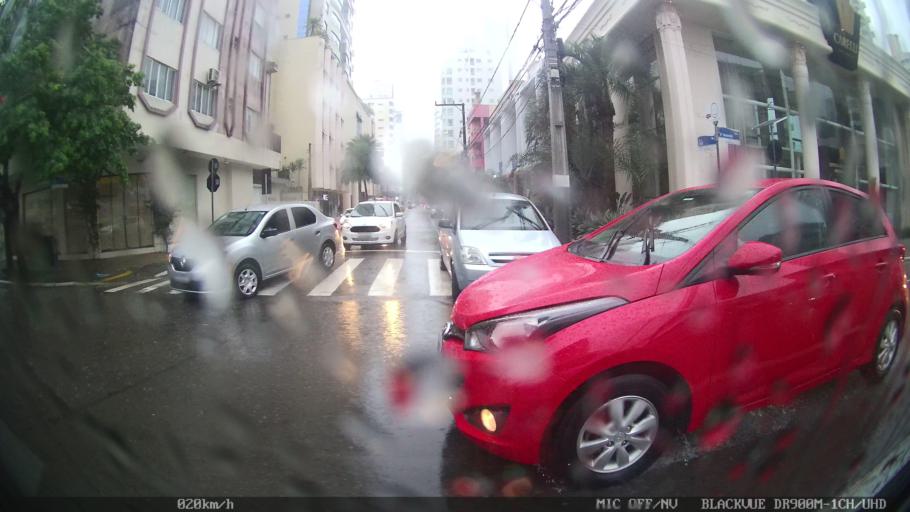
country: BR
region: Santa Catarina
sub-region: Balneario Camboriu
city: Balneario Camboriu
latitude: -26.9905
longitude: -48.6389
